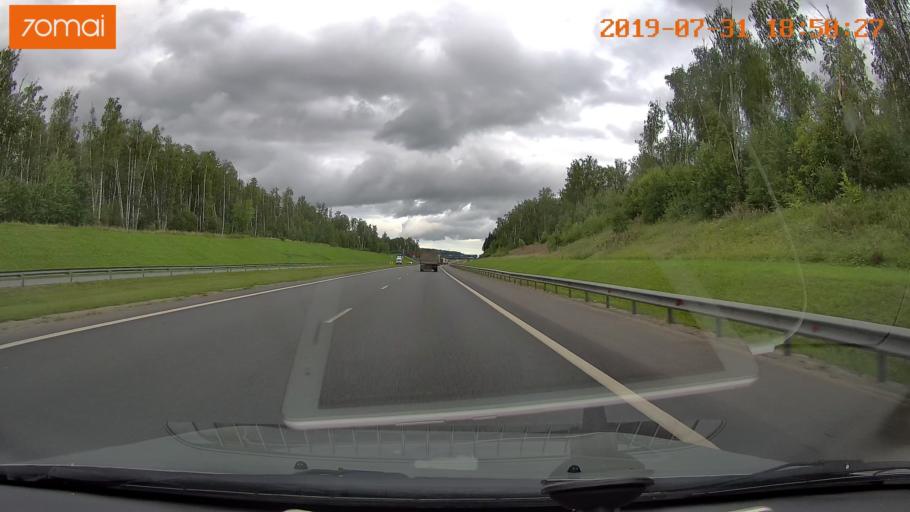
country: RU
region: Moskovskaya
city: Troitskoye
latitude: 55.2286
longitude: 38.5824
